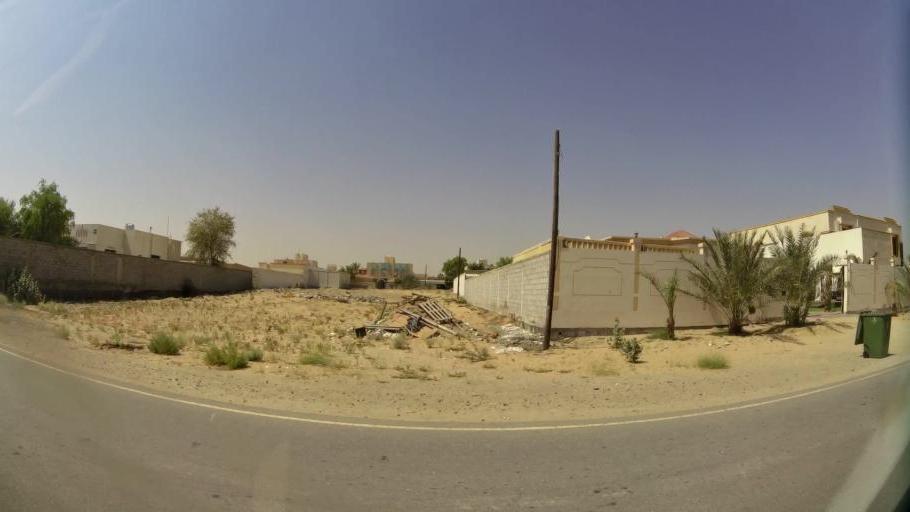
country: AE
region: Ajman
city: Ajman
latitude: 25.3976
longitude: 55.5387
